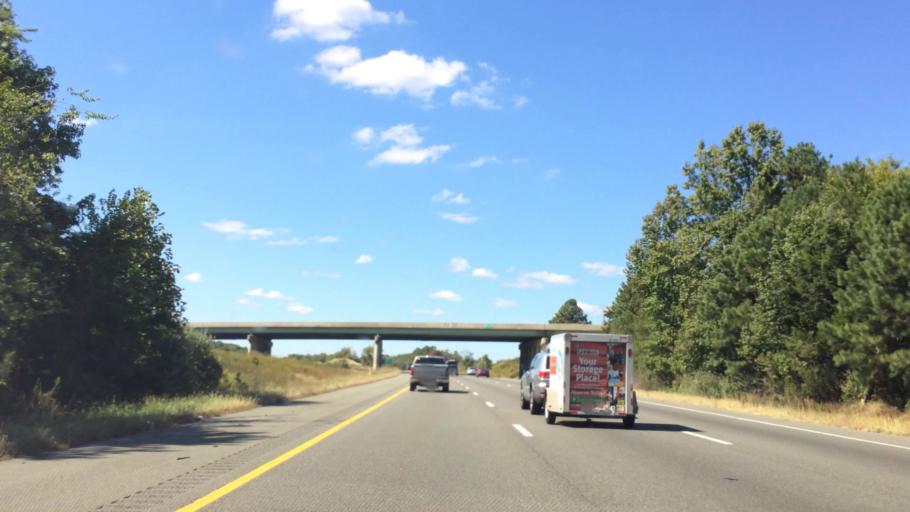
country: US
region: Virginia
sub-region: Henrico County
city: Glen Allen
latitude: 37.6816
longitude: -77.5201
